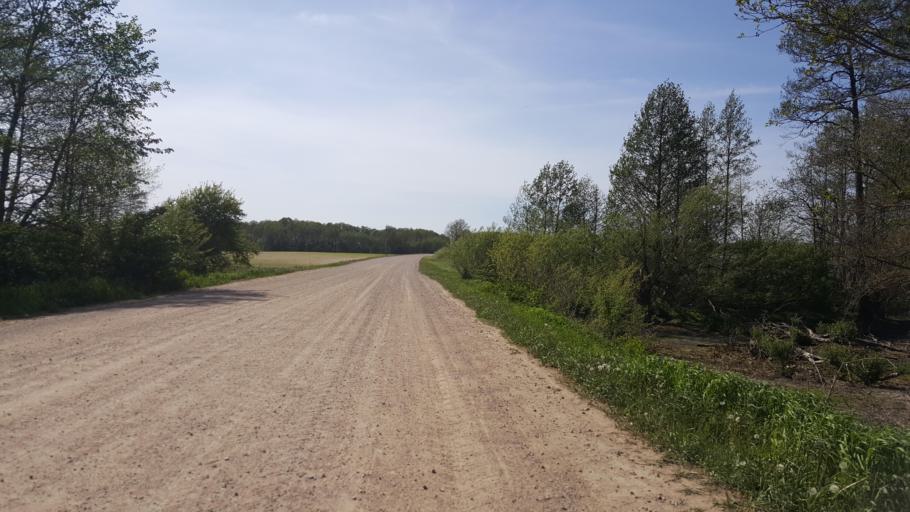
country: BY
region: Brest
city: Zhabinka
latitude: 52.3129
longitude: 24.0360
